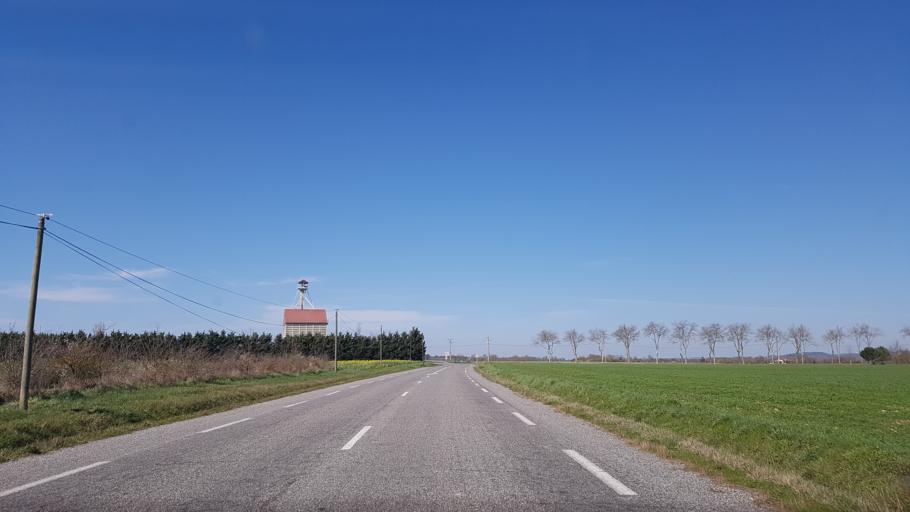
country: FR
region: Midi-Pyrenees
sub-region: Departement de l'Ariege
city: Mazeres
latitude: 43.2335
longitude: 1.6595
